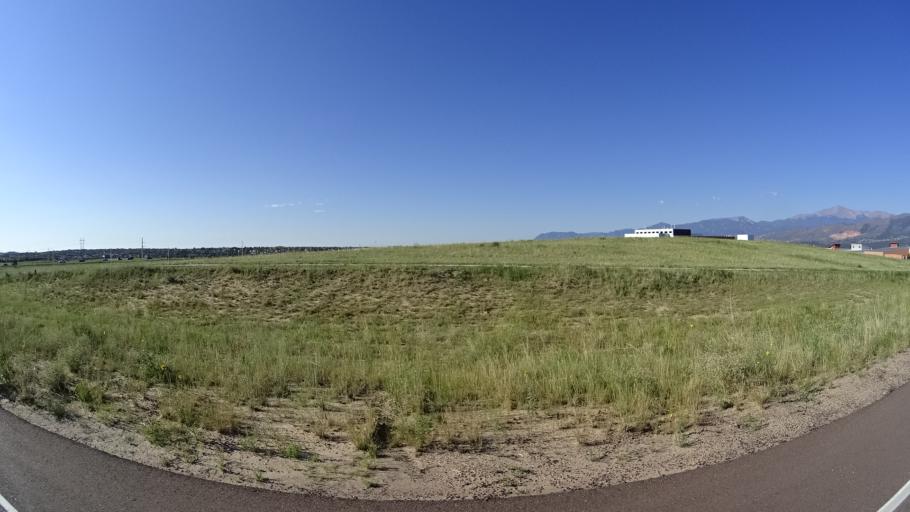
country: US
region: Colorado
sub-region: El Paso County
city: Gleneagle
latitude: 38.9948
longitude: -104.7875
